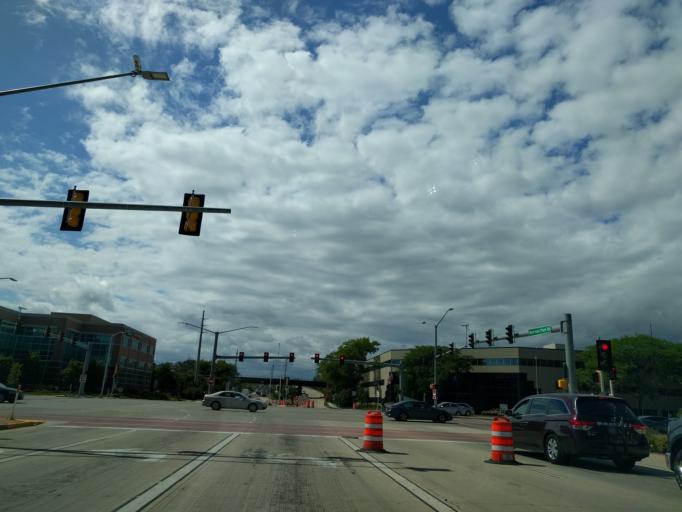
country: US
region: Wisconsin
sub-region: Waukesha County
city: Elm Grove
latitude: 43.0456
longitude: -88.0466
